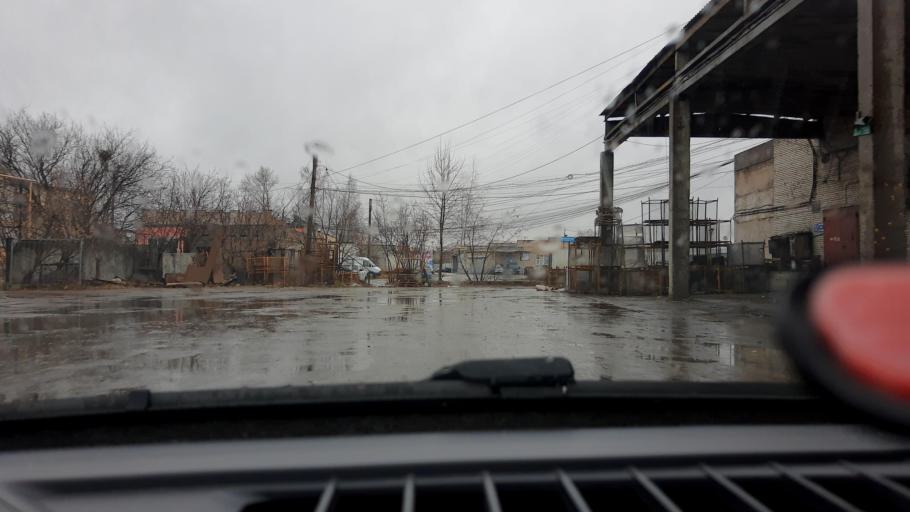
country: RU
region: Nizjnij Novgorod
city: Gorbatovka
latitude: 56.3356
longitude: 43.8110
